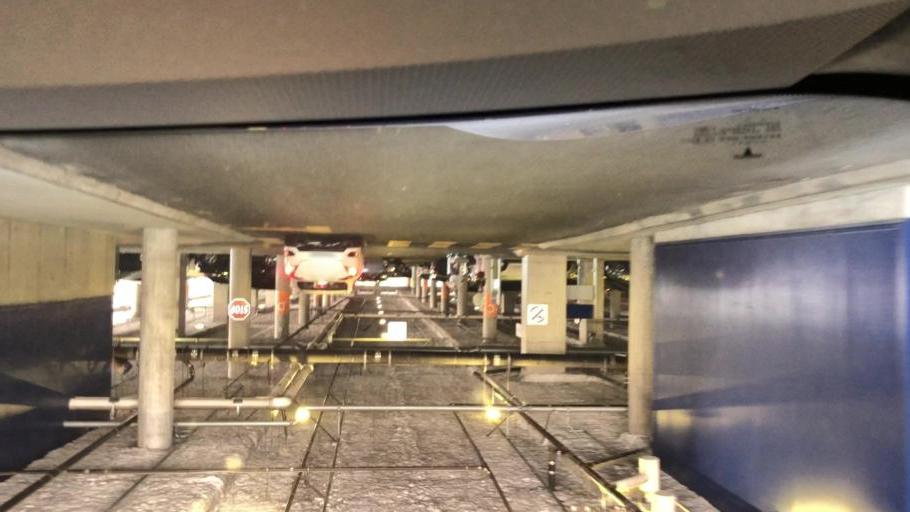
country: CA
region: British Columbia
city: Richmond
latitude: 49.1889
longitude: -123.0800
